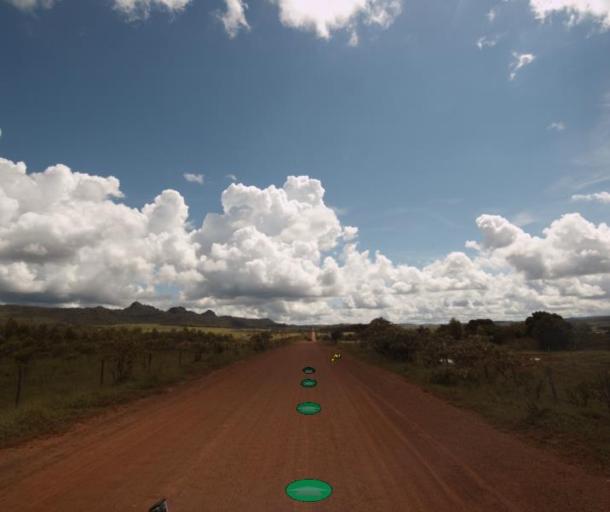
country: BR
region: Goias
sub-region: Pirenopolis
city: Pirenopolis
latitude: -15.7814
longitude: -48.8102
